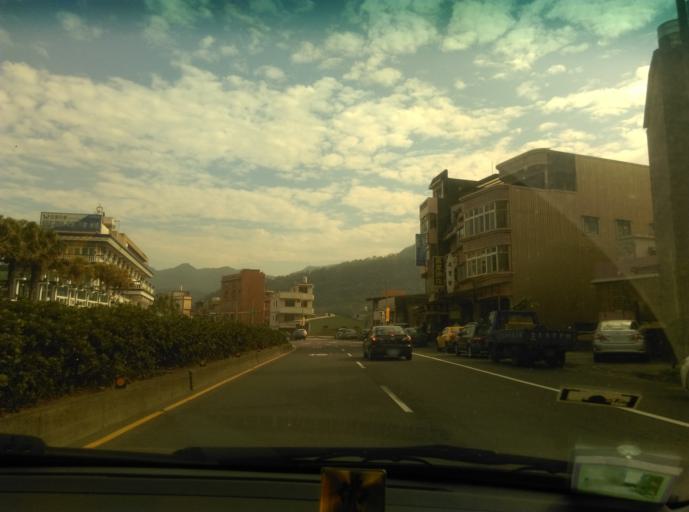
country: TW
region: Taiwan
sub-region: Keelung
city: Keelung
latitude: 25.1810
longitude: 121.6895
